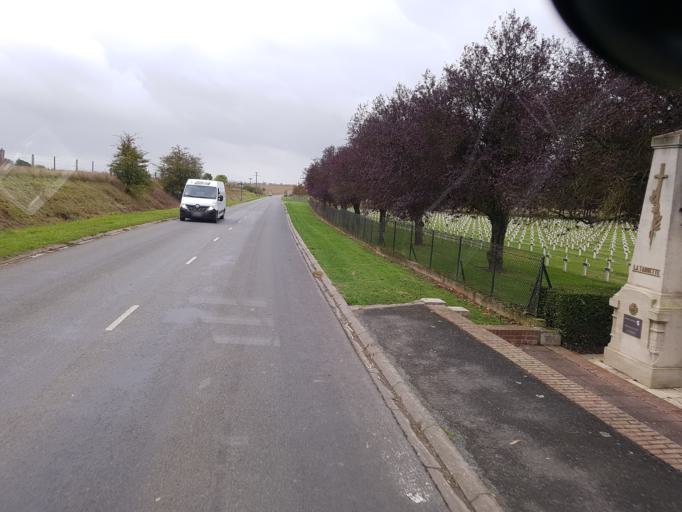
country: FR
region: Nord-Pas-de-Calais
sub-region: Departement du Pas-de-Calais
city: Neuville-Saint-Vaast
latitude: 50.3496
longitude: 2.7481
